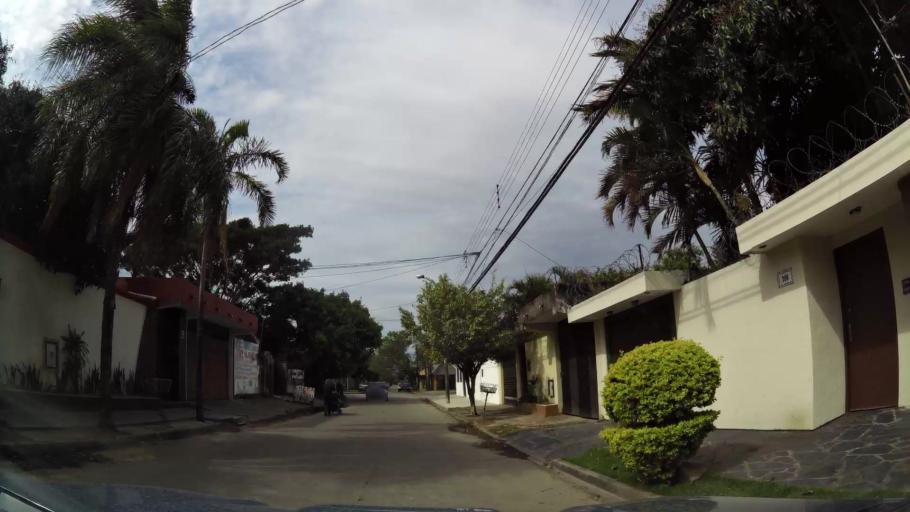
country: BO
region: Santa Cruz
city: Santa Cruz de la Sierra
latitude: -17.7918
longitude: -63.2021
